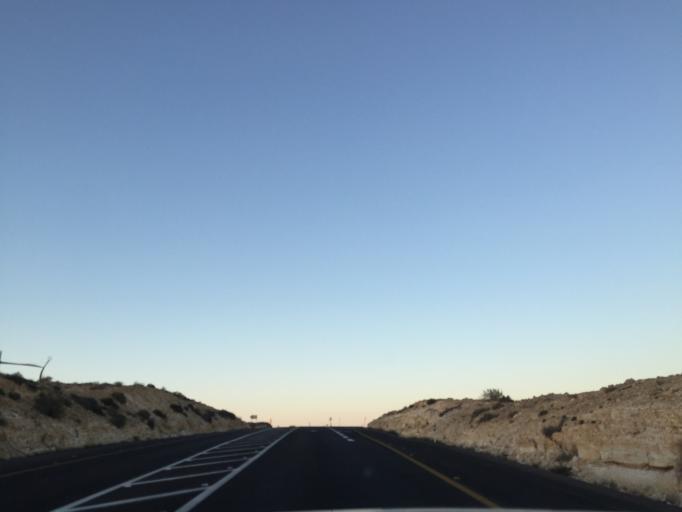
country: IL
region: Southern District
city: Midreshet Ben-Gurion
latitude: 30.8868
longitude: 34.7924
